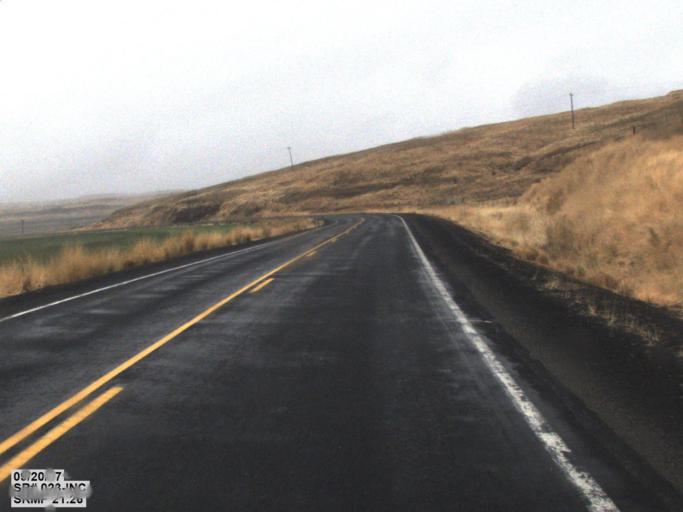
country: US
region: Washington
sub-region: Spokane County
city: Cheney
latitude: 47.1139
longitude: -117.7144
